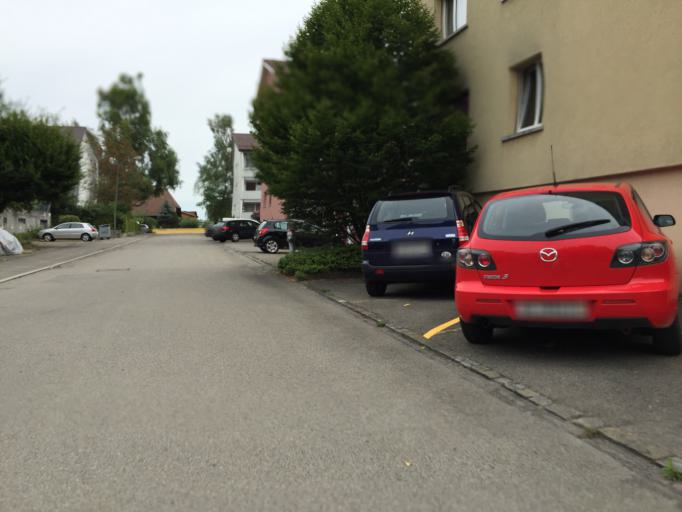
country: CH
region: Bern
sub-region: Bern-Mittelland District
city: Koniz
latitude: 46.9217
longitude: 7.4213
